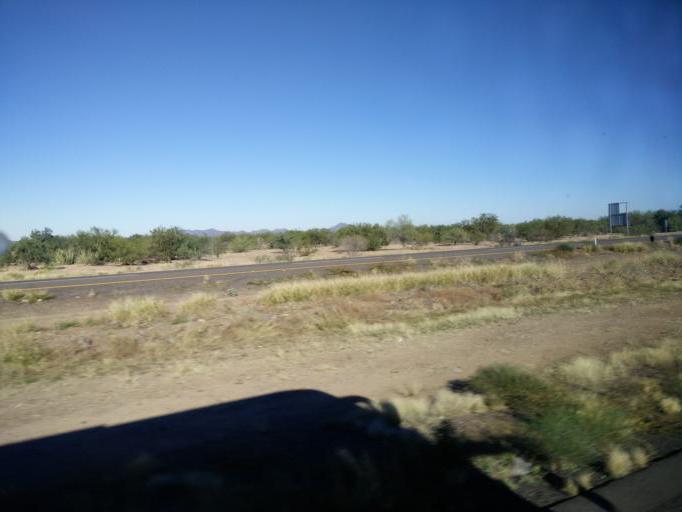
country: MX
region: Sonora
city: Hermosillo
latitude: 28.7285
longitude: -110.9790
